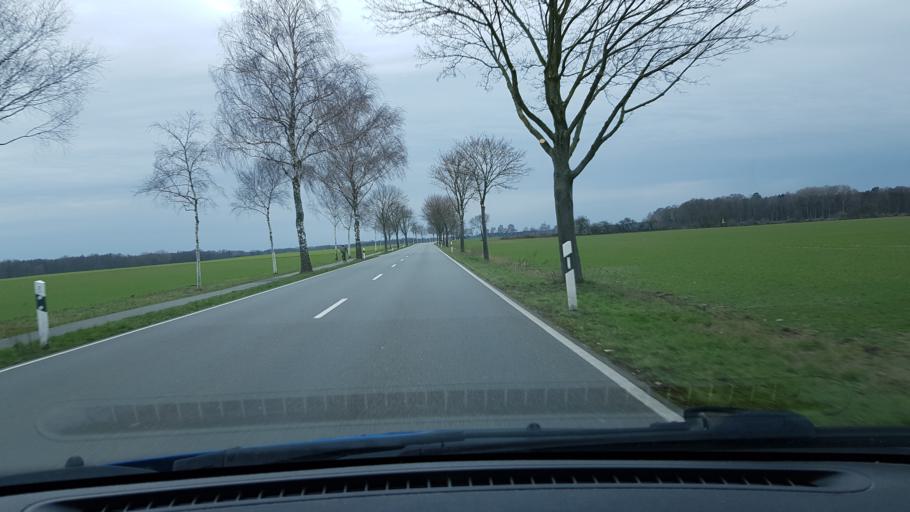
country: DE
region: Lower Saxony
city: Ratzlingen
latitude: 52.9746
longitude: 10.6501
